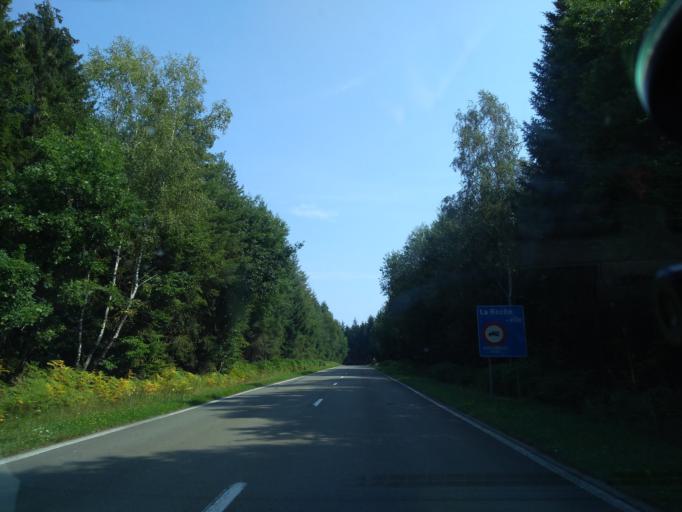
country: BE
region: Wallonia
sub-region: Province du Luxembourg
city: Tenneville
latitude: 50.1386
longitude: 5.4979
